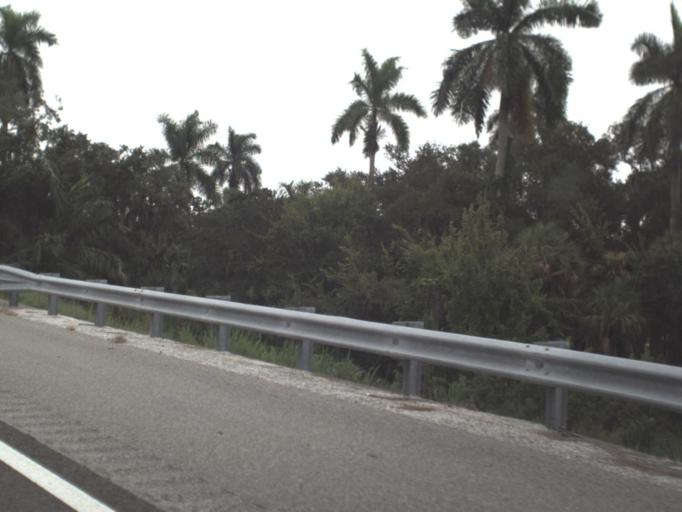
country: US
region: Florida
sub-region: Manatee County
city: Memphis
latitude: 27.5808
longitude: -82.5657
